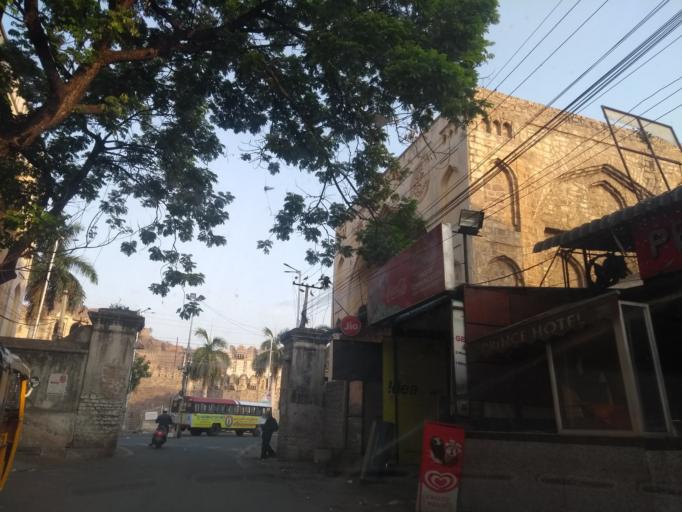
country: IN
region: Telangana
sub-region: Hyderabad
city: Hyderabad
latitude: 17.3837
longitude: 78.4038
